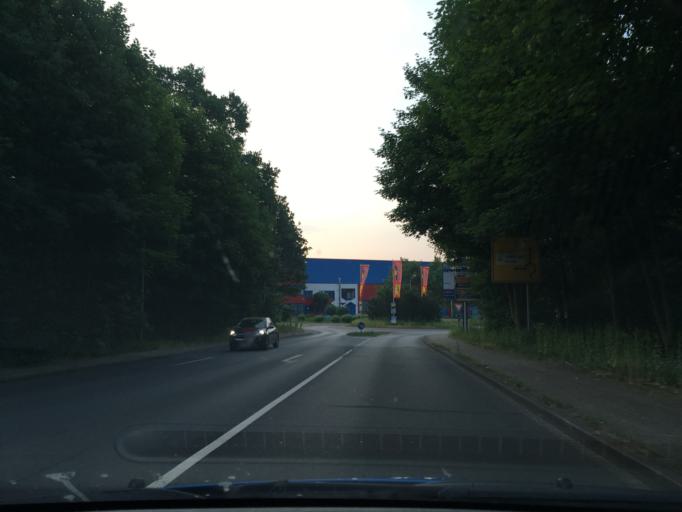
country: DE
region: Lower Saxony
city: Buchholz in der Nordheide
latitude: 53.3480
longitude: 9.8556
